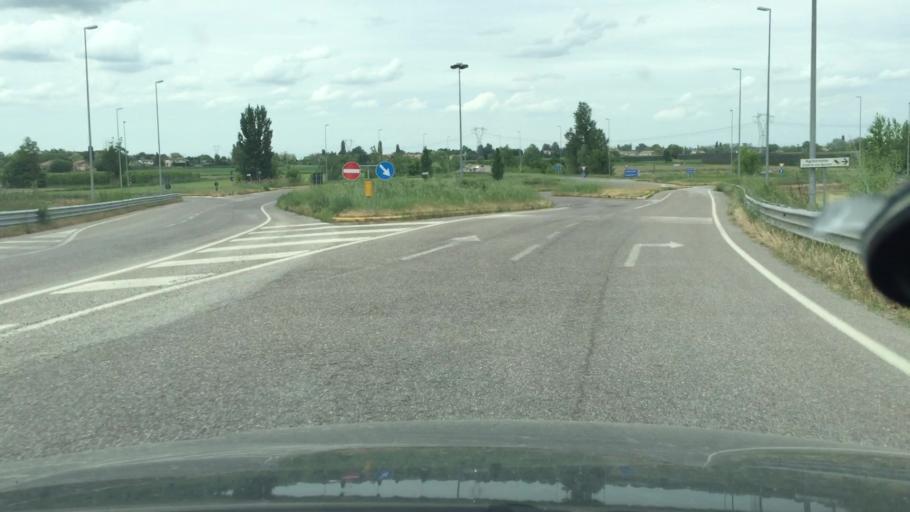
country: IT
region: Emilia-Romagna
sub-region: Provincia di Ferrara
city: Cona
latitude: 44.8038
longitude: 11.7206
